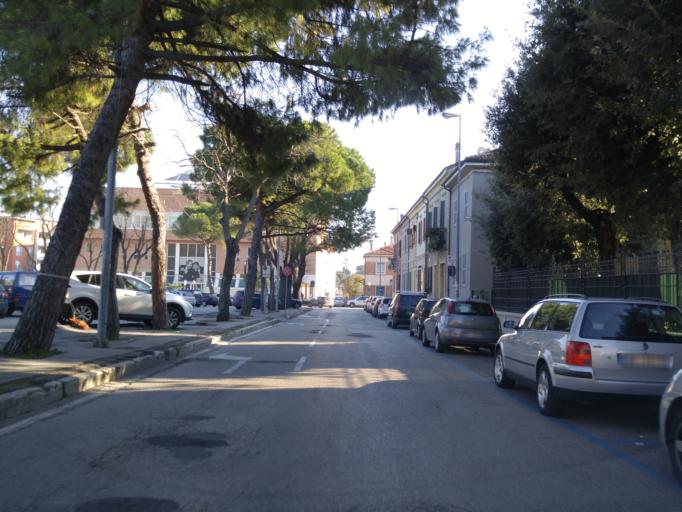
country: IT
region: The Marches
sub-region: Provincia di Pesaro e Urbino
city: Pesaro
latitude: 43.9062
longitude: 12.9119
